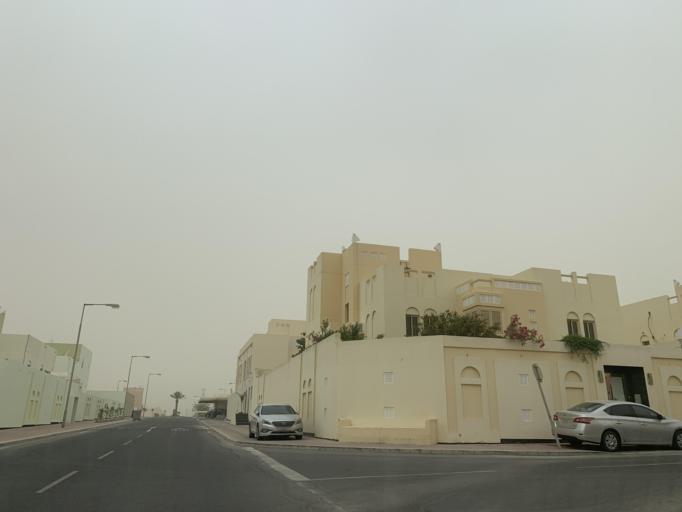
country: BH
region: Central Governorate
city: Madinat Hamad
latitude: 26.1306
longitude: 50.5115
